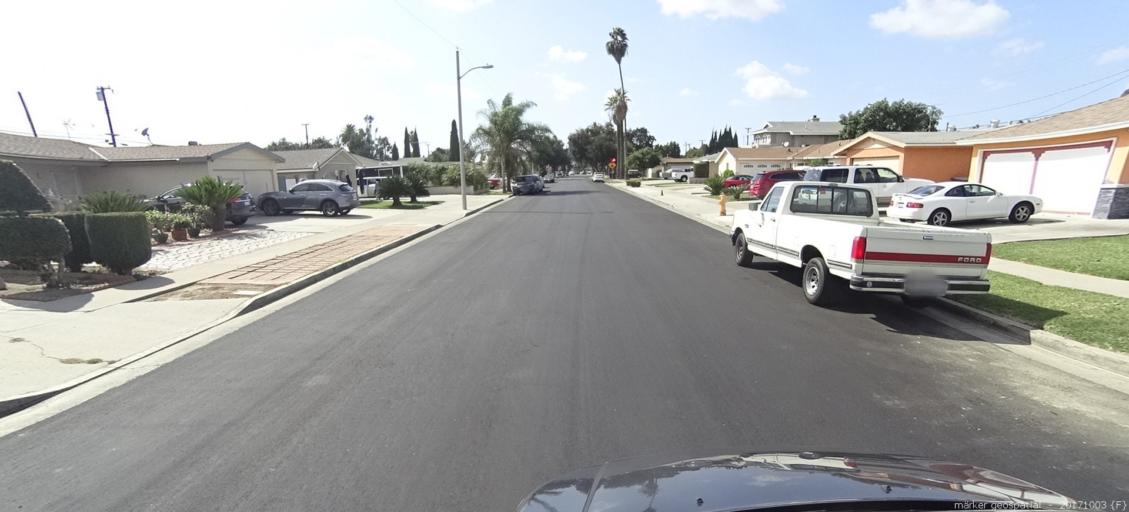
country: US
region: California
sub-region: Orange County
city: Santa Ana
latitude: 33.7694
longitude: -117.8962
